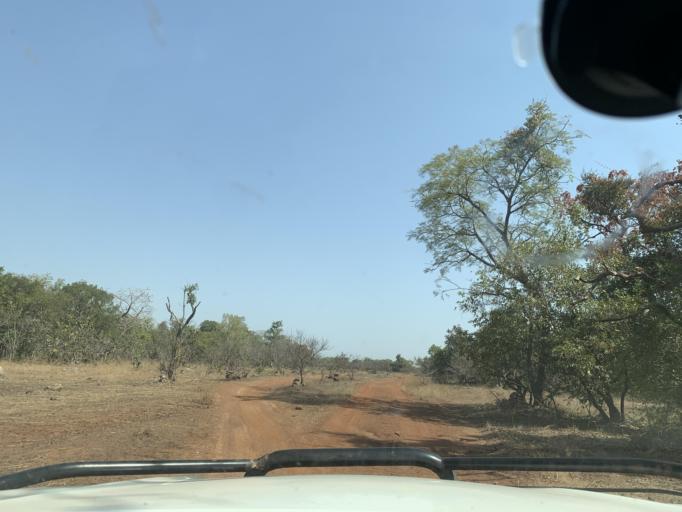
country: ML
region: Sikasso
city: Kolondieba
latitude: 10.8881
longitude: -6.7591
